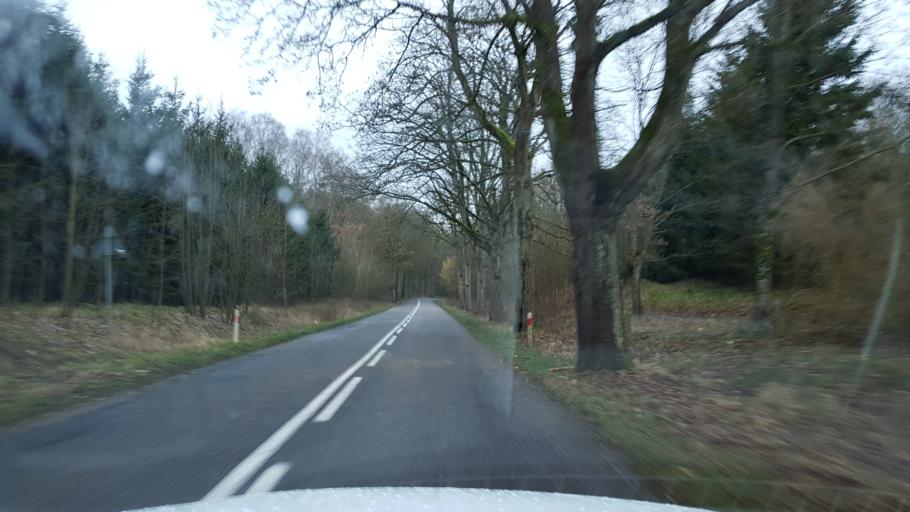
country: PL
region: West Pomeranian Voivodeship
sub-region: Powiat lobeski
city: Lobez
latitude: 53.6536
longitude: 15.5888
